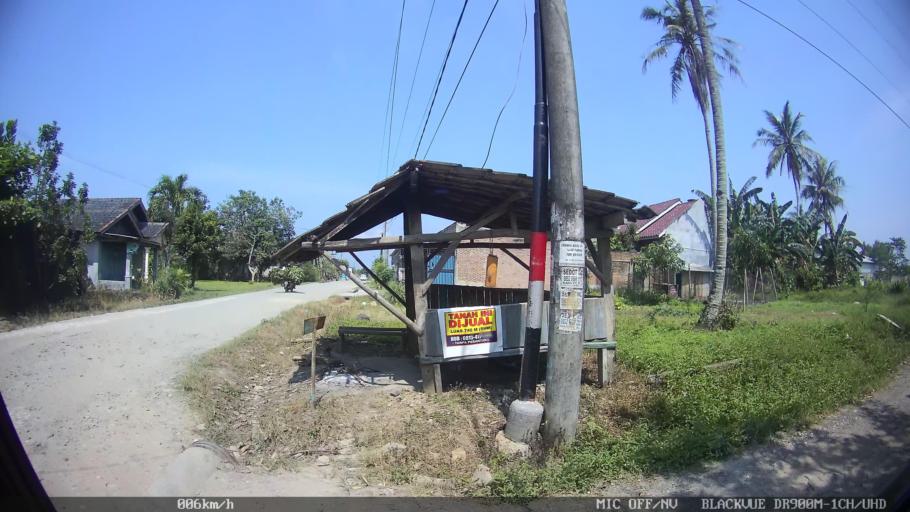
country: ID
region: Lampung
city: Natar
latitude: -5.2664
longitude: 105.1968
